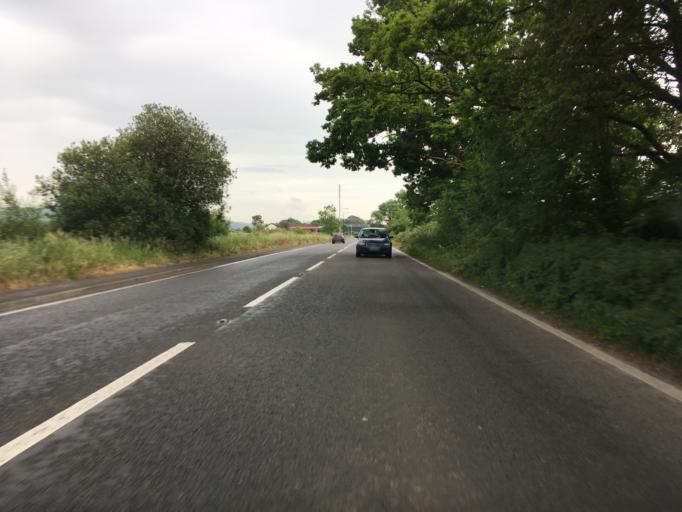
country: GB
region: England
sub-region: North Somerset
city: Yatton
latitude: 51.3727
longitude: -2.8272
